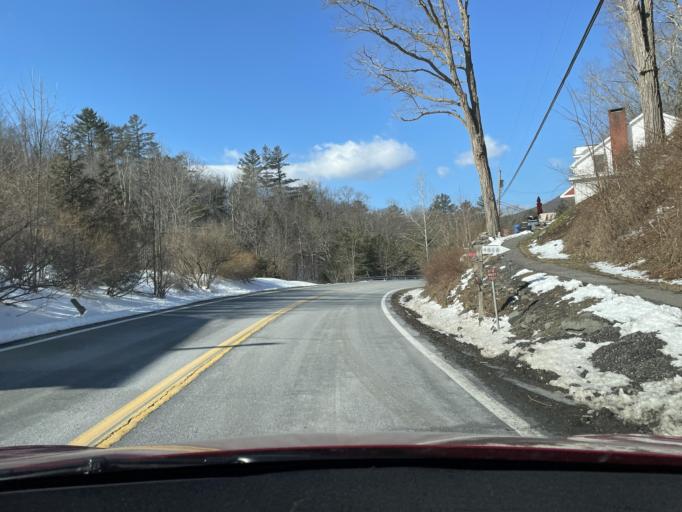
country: US
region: New York
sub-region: Ulster County
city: Shokan
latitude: 42.0652
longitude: -74.2406
